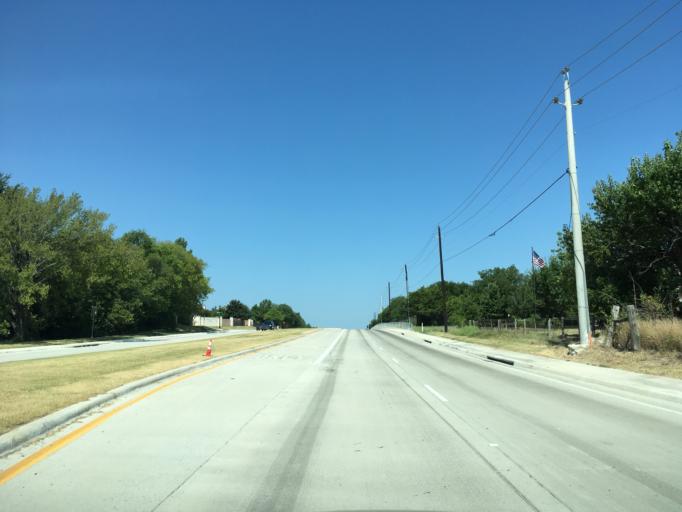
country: US
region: Texas
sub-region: Collin County
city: Fairview
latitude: 33.1289
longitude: -96.6154
